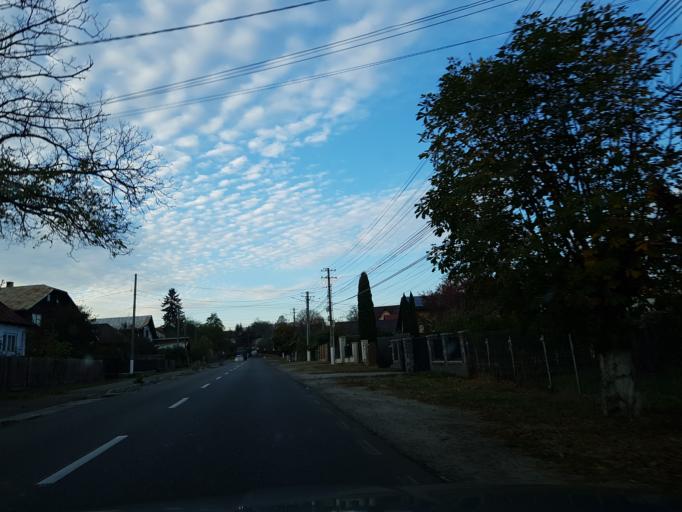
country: RO
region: Prahova
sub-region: Oras Breaza
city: Breaza de Sus
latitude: 45.2025
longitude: 25.6507
